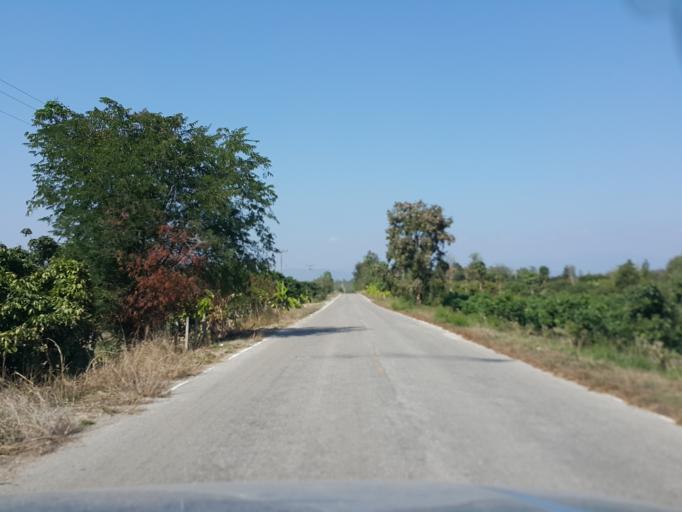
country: TH
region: Chiang Mai
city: Mae Wang
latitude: 18.5458
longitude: 98.7965
